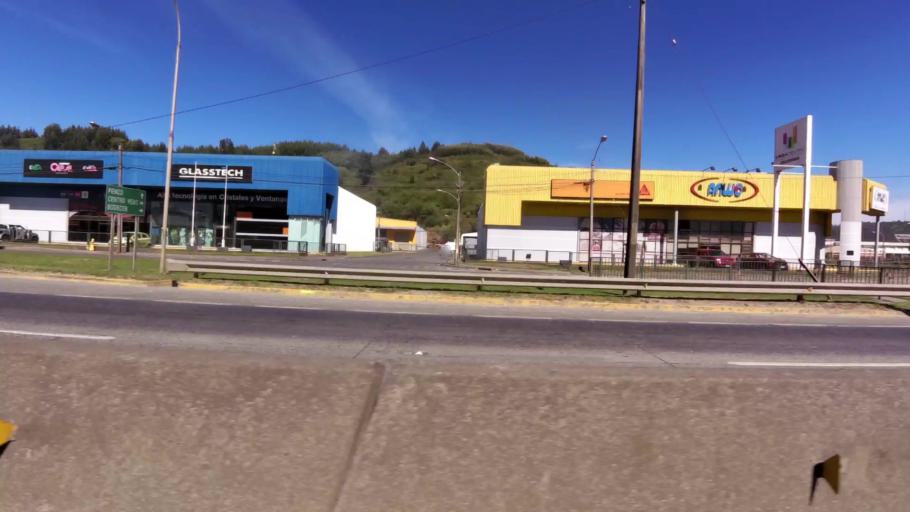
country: CL
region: Biobio
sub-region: Provincia de Concepcion
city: Concepcion
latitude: -36.8085
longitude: -73.0252
